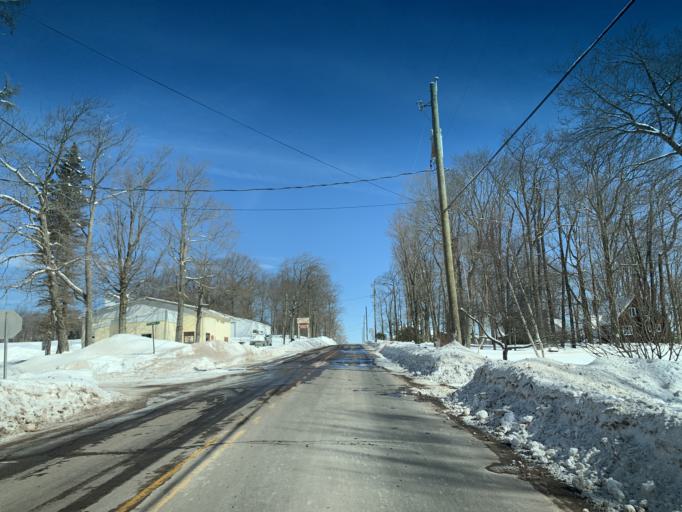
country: US
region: Pennsylvania
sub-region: Somerset County
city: Meyersdale
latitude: 39.7274
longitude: -79.1577
